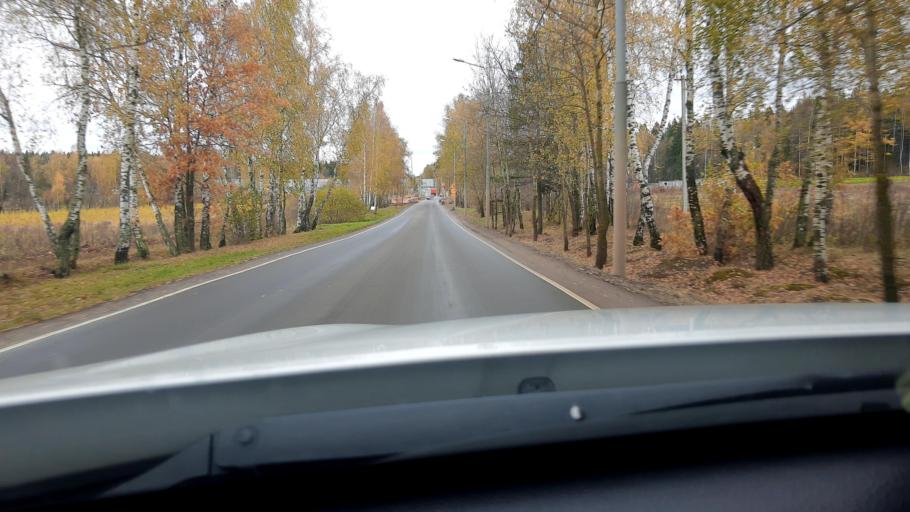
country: RU
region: Moskovskaya
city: Annino
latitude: 55.5747
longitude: 37.2368
